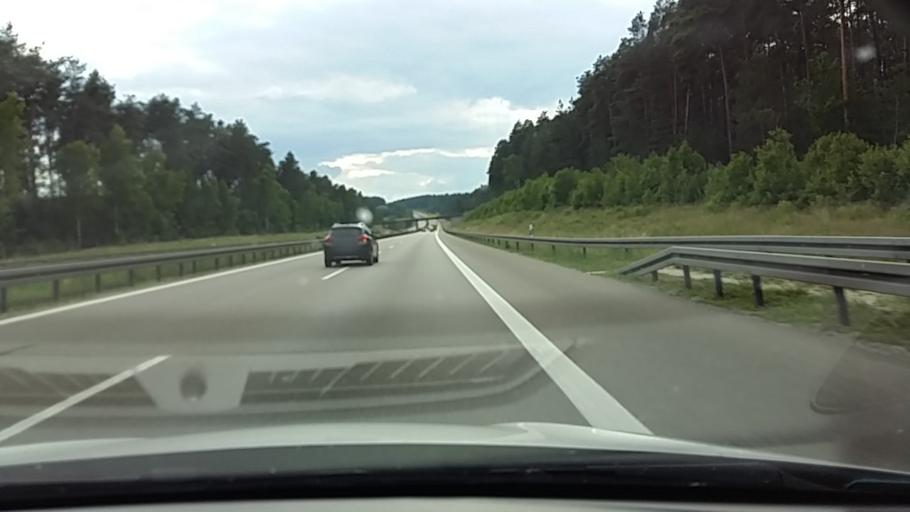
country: DE
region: Bavaria
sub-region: Upper Palatinate
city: Ebermannsdorf
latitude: 49.3982
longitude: 11.9579
